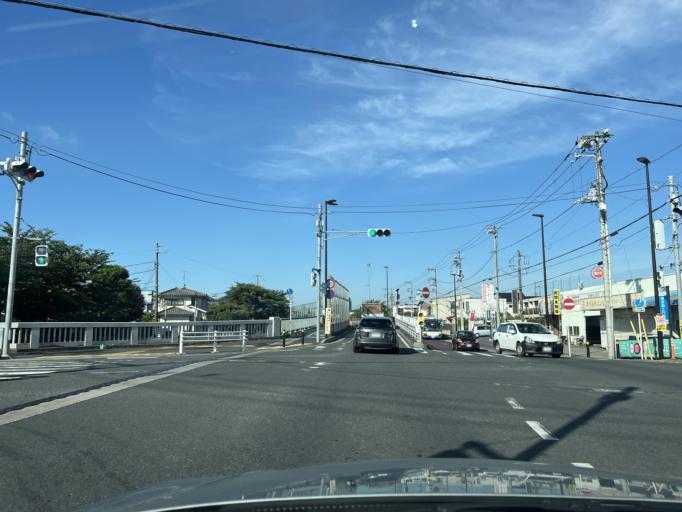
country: JP
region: Chiba
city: Funabashi
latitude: 35.7326
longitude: 139.9427
